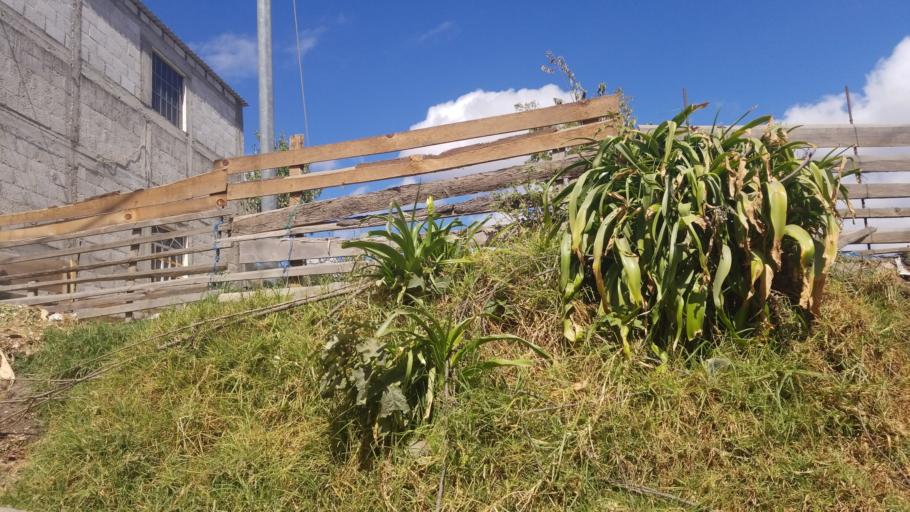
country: GT
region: Quetzaltenango
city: Almolonga
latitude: 14.7874
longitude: -91.5453
